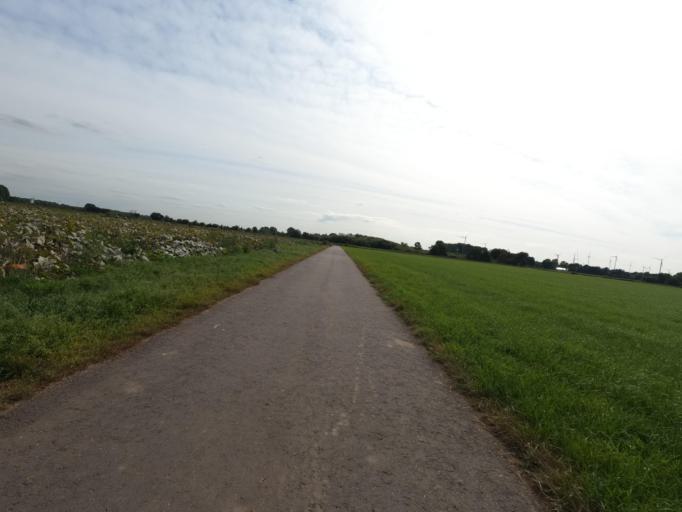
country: DE
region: North Rhine-Westphalia
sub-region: Regierungsbezirk Koln
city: Linnich
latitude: 51.0099
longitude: 6.2540
